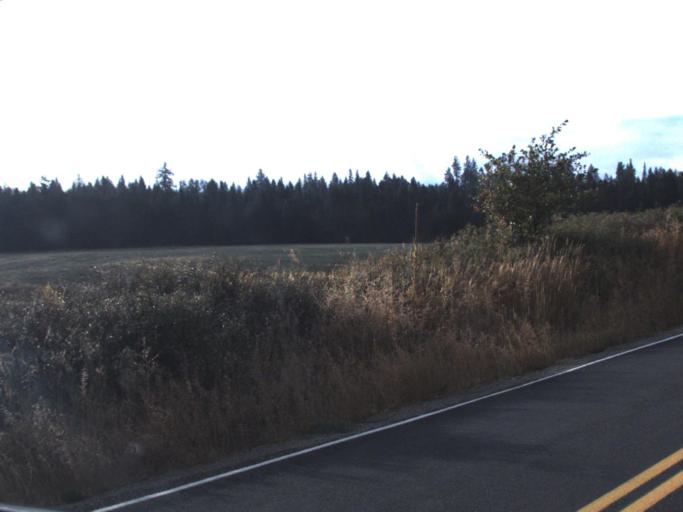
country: US
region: Washington
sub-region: Stevens County
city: Chewelah
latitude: 48.0819
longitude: -117.7579
